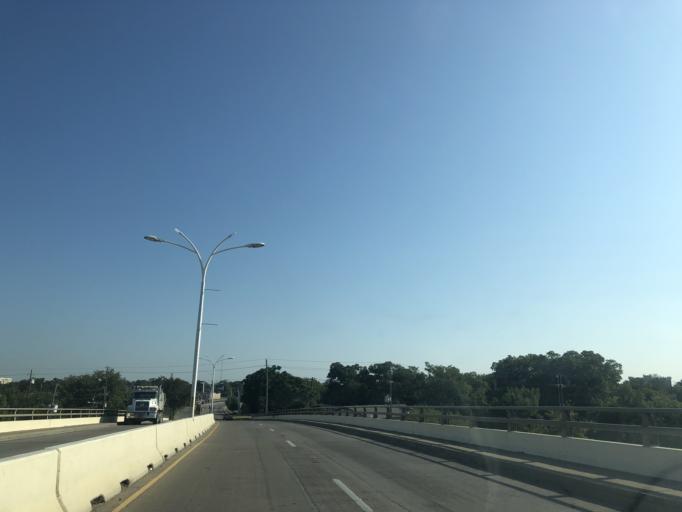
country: US
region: Texas
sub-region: Dallas County
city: Dallas
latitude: 32.7561
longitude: -96.7803
